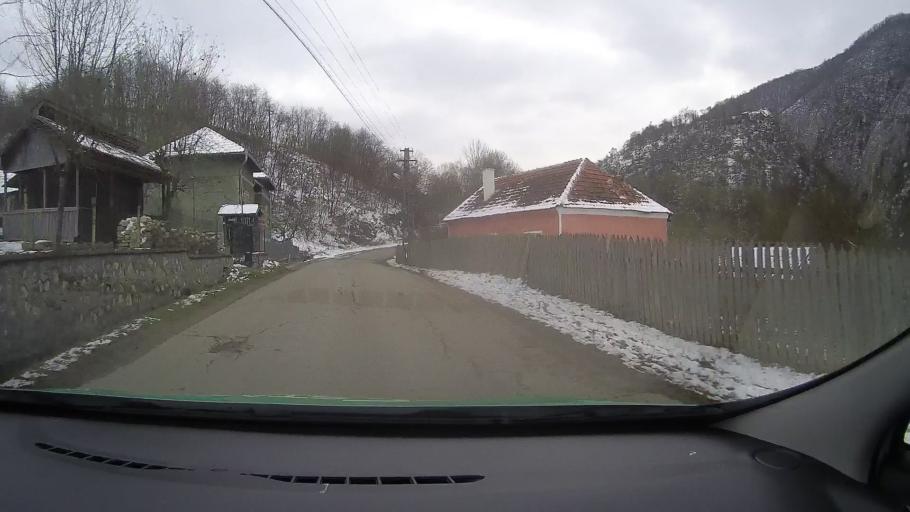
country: RO
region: Hunedoara
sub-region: Comuna Balsa
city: Balsa
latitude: 46.0196
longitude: 23.1459
